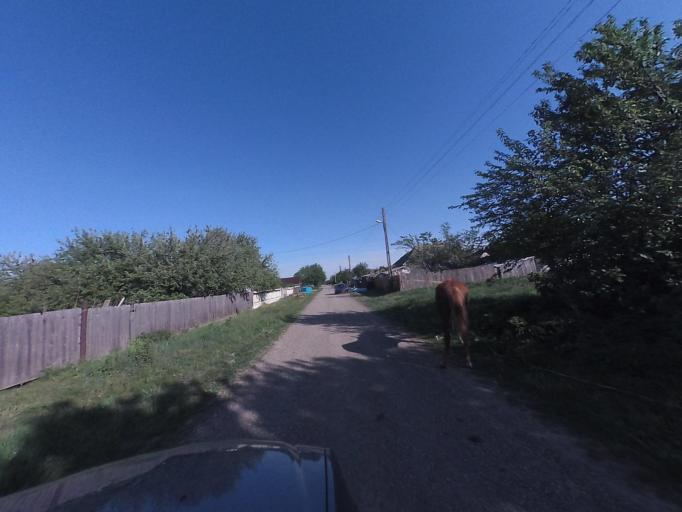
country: RO
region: Neamt
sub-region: Comuna Dulcesti
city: Dulcesti
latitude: 47.0054
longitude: 26.7705
